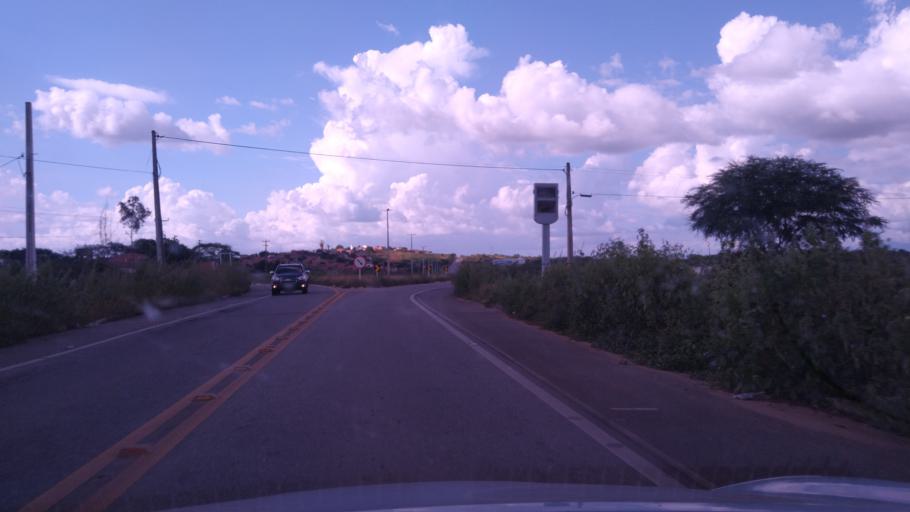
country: BR
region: Ceara
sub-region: Caninde
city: Caninde
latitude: -4.3802
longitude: -39.3098
